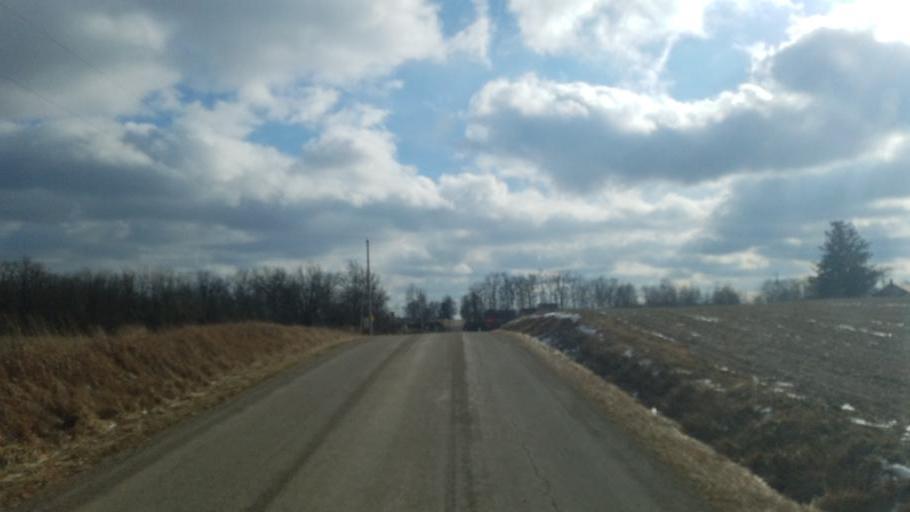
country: US
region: Ohio
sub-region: Morrow County
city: Mount Gilead
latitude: 40.6125
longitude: -82.7474
